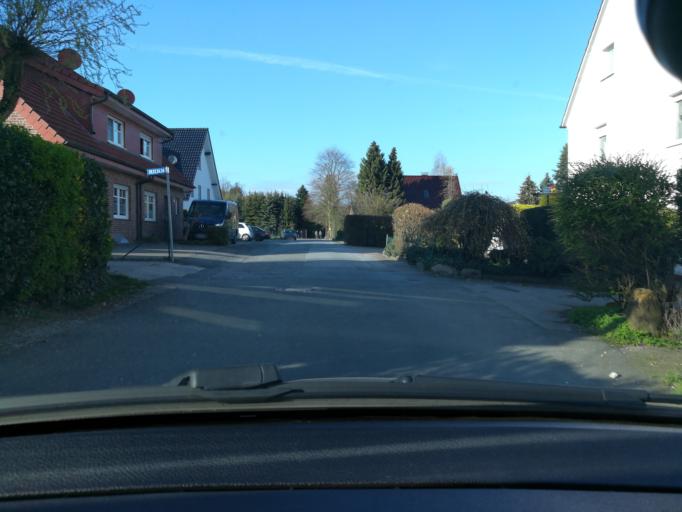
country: DE
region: North Rhine-Westphalia
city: Borgholzhausen
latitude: 52.0998
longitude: 8.2975
